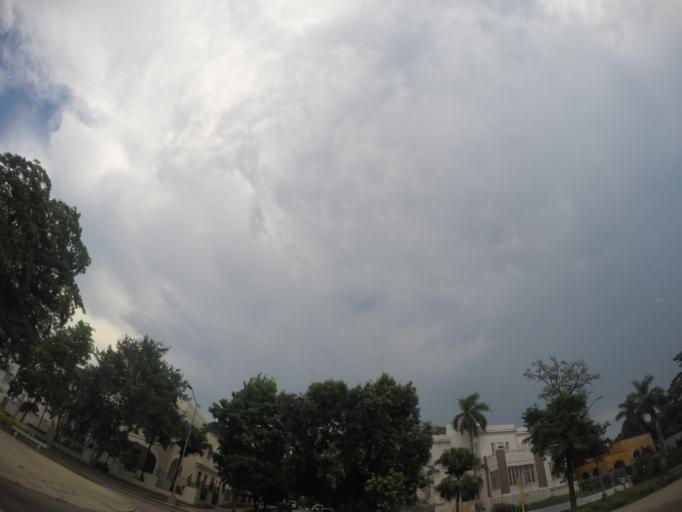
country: CU
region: La Habana
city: Havana
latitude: 23.1219
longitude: -82.4214
